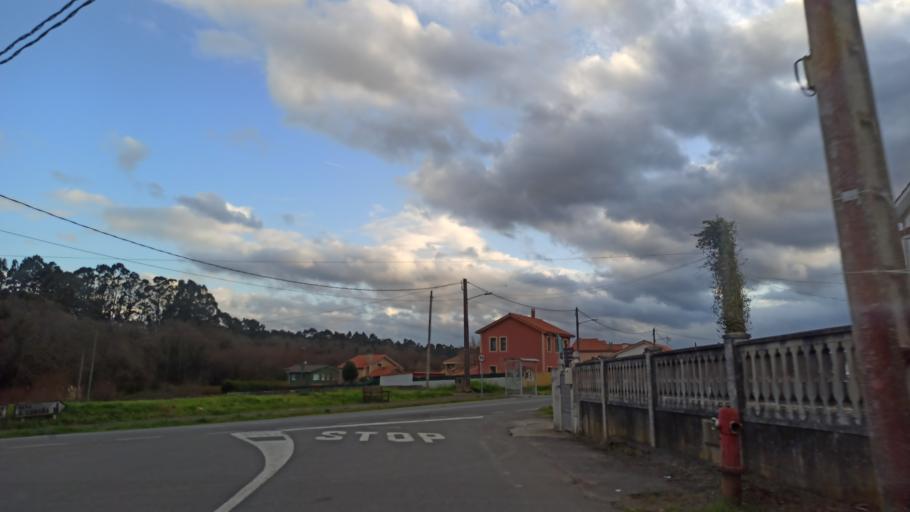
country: ES
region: Galicia
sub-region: Provincia da Coruna
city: Oleiros
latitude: 43.3865
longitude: -8.3215
